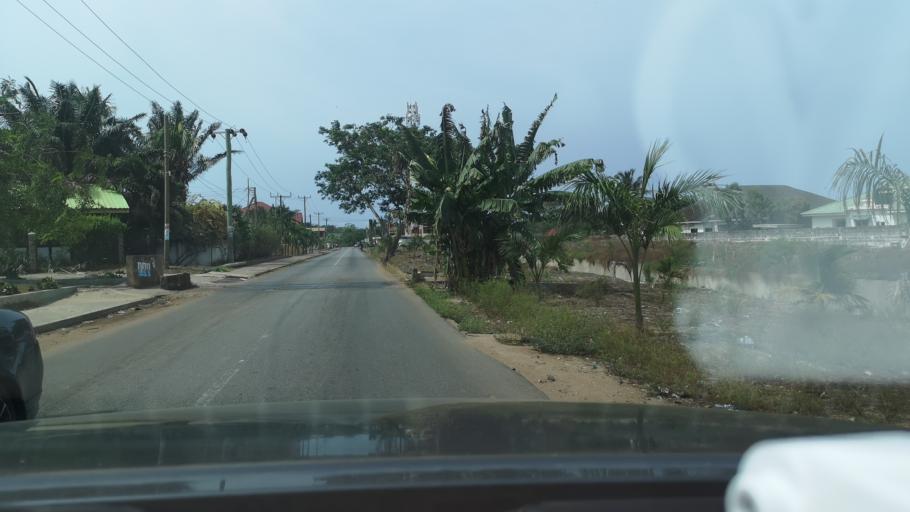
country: GH
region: Greater Accra
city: Tema
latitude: 5.6543
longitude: -0.0213
